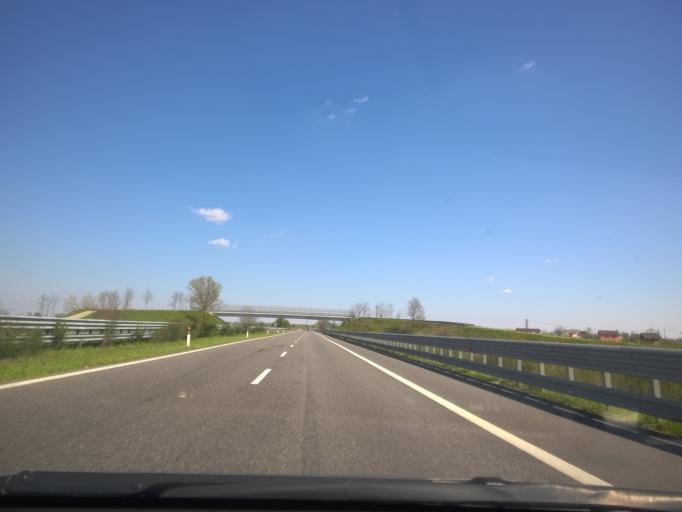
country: IT
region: Emilia-Romagna
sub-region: Provincia di Piacenza
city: Pontenure
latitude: 45.0497
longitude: 9.7801
